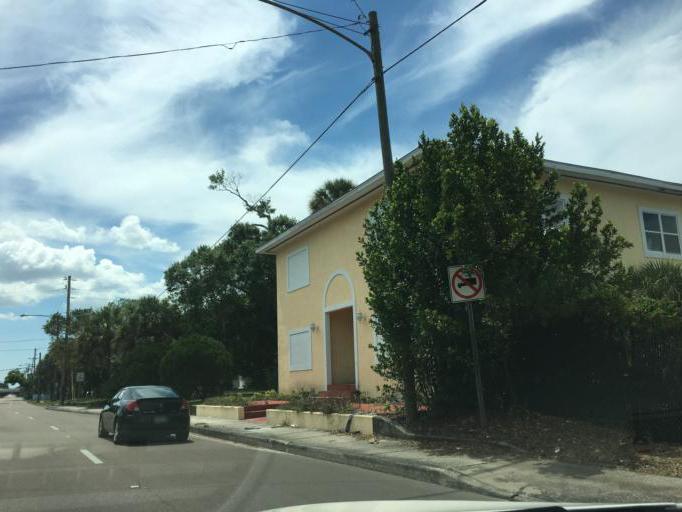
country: US
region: Florida
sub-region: Pinellas County
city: Saint Petersburg
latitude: 27.7811
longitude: -82.6551
